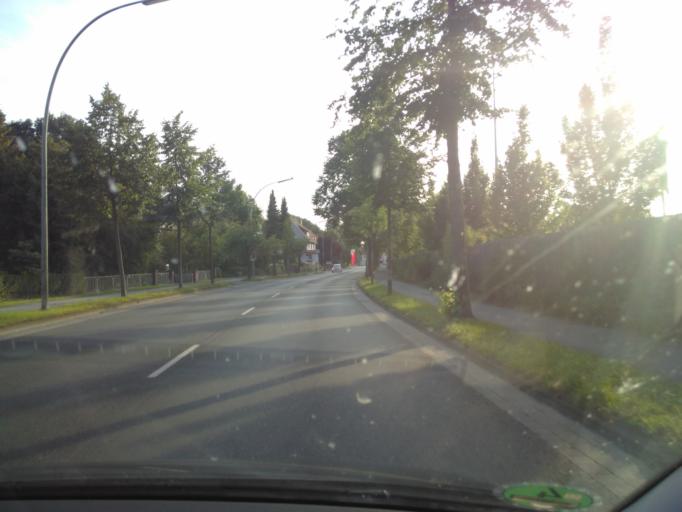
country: DE
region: North Rhine-Westphalia
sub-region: Regierungsbezirk Detmold
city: Rheda-Wiedenbruck
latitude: 51.8553
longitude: 8.3017
